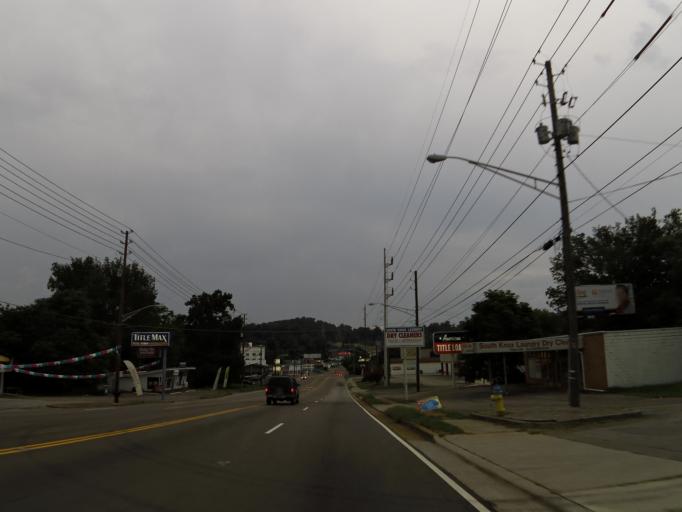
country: US
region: Tennessee
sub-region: Knox County
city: Knoxville
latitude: 35.9384
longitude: -83.9084
